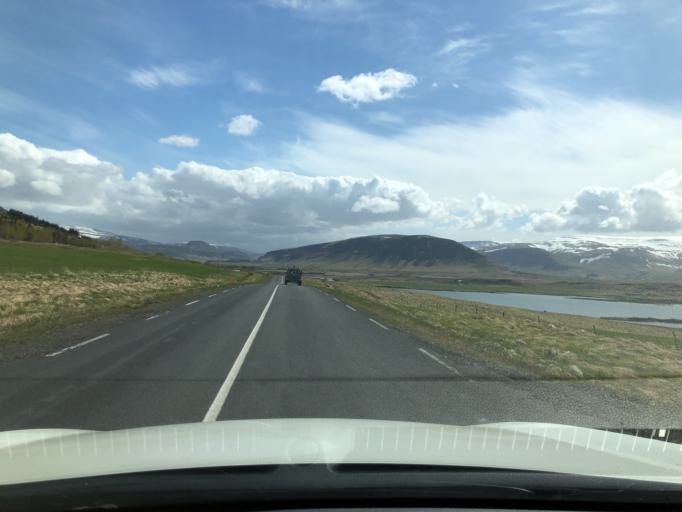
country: IS
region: Capital Region
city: Mosfellsbaer
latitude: 64.3535
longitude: -21.6398
